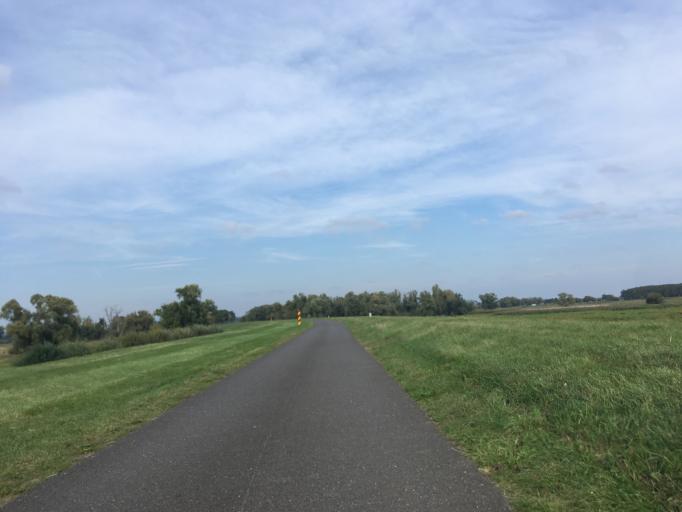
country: DE
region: Brandenburg
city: Schoneberg
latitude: 52.9394
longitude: 14.1376
